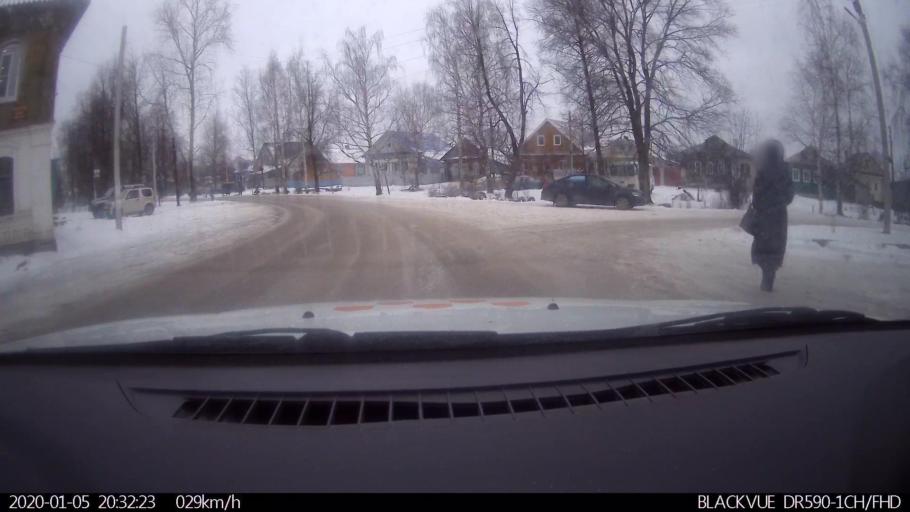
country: RU
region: Nizjnij Novgorod
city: Lukino
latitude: 56.4119
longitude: 43.7289
